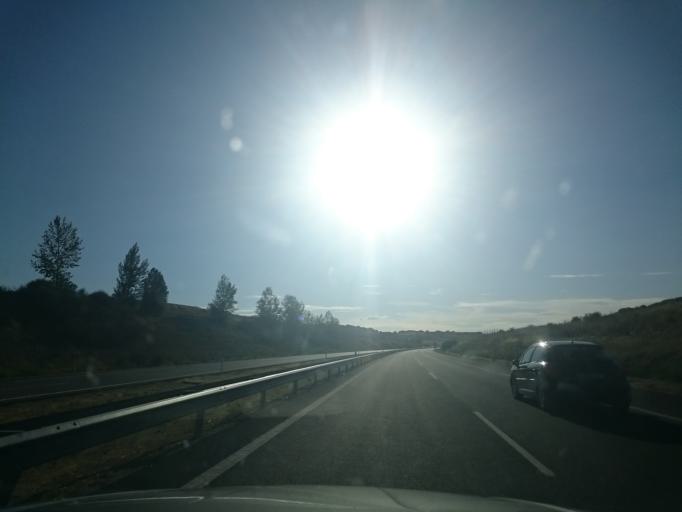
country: ES
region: Castille and Leon
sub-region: Provincia de Burgos
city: Villanueva de Argano
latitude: 42.3808
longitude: -3.9568
